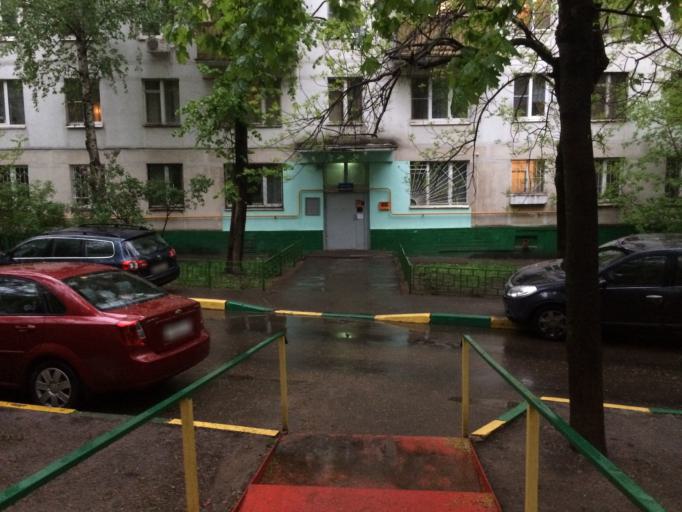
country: RU
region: Moskovskaya
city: Semenovskoye
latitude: 55.6741
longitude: 37.5547
